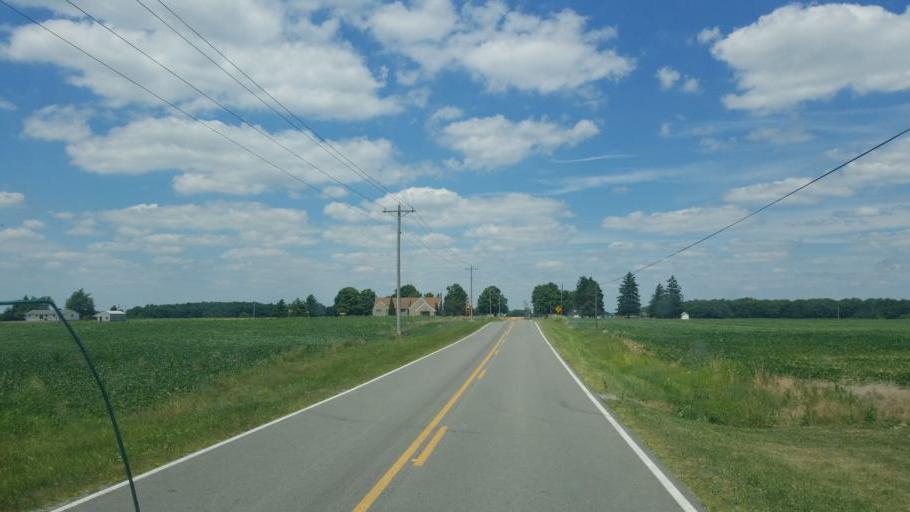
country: US
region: Ohio
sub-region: Williams County
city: Edgerton
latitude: 41.4232
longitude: -84.7102
